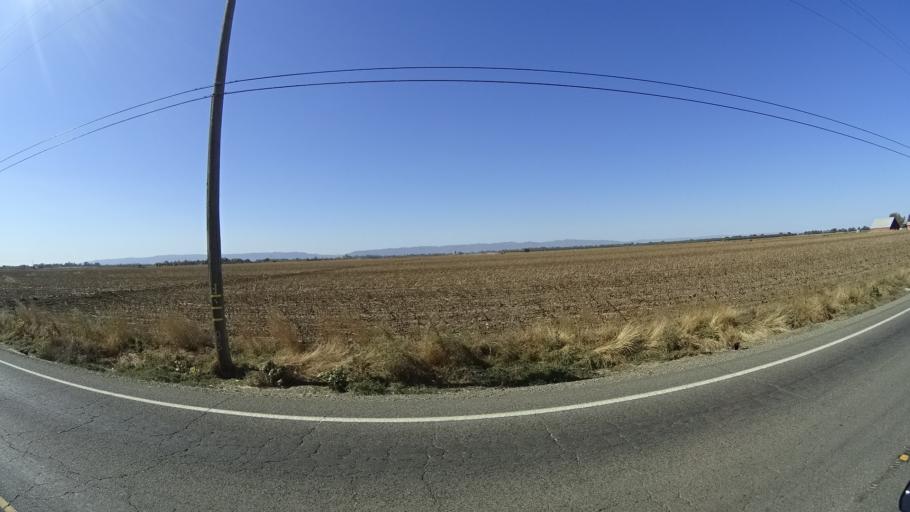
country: US
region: California
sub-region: Yolo County
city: Davis
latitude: 38.5659
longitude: -121.8033
